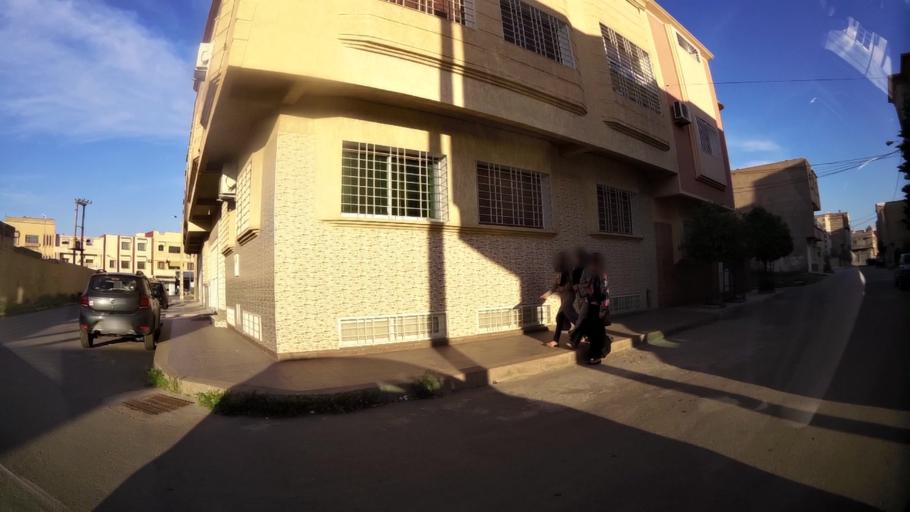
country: MA
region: Oriental
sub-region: Oujda-Angad
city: Oujda
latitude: 34.7029
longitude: -1.9145
